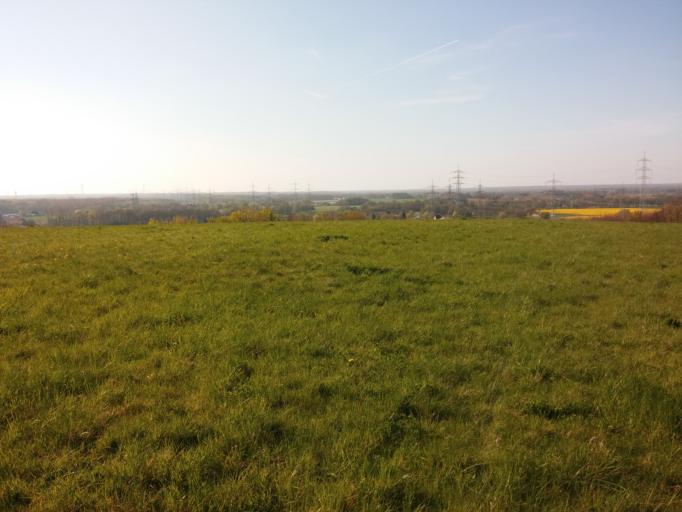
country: DE
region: North Rhine-Westphalia
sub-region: Regierungsbezirk Munster
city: Gladbeck
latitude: 51.6194
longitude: 7.0211
